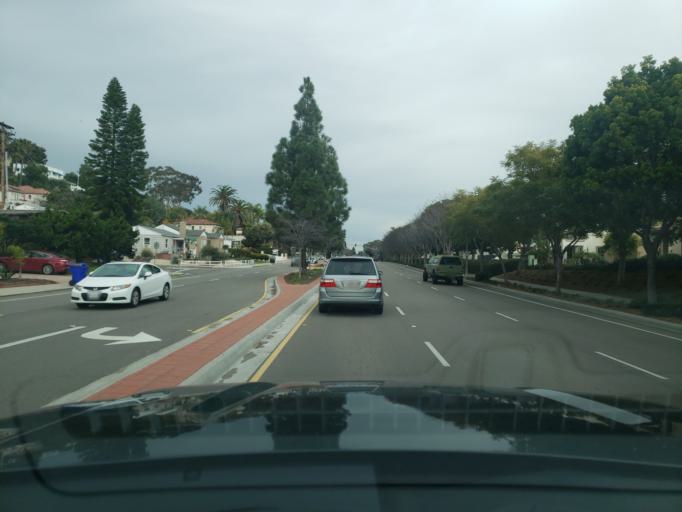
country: US
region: California
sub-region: San Diego County
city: Coronado
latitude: 32.7330
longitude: -117.2221
